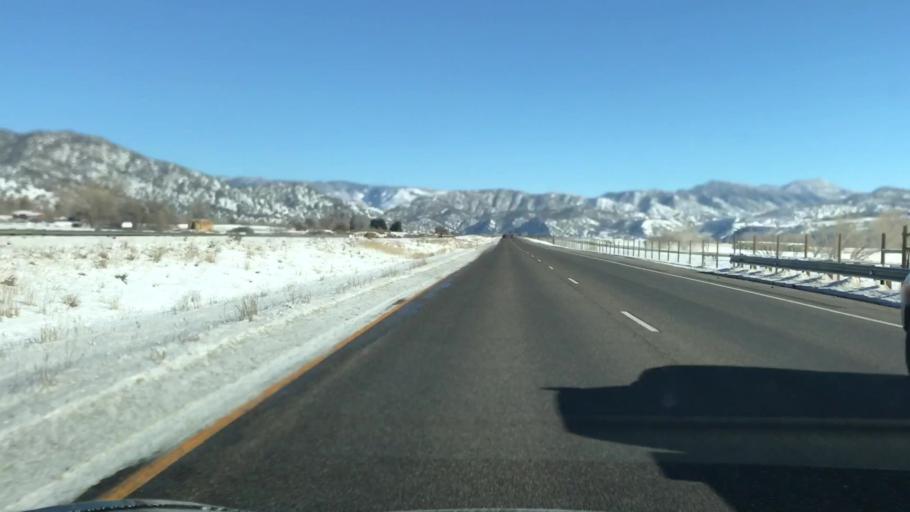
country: US
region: Colorado
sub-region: Garfield County
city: New Castle
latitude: 39.5522
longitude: -107.5878
